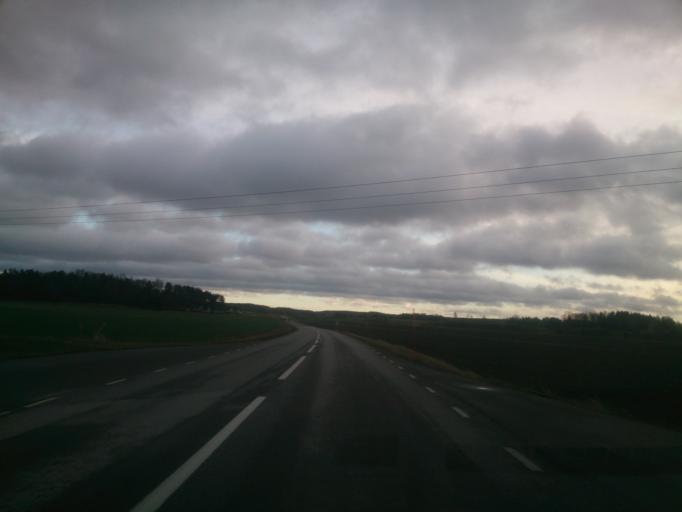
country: SE
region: OEstergoetland
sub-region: Norrkopings Kommun
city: Krokek
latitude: 58.5779
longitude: 16.3951
